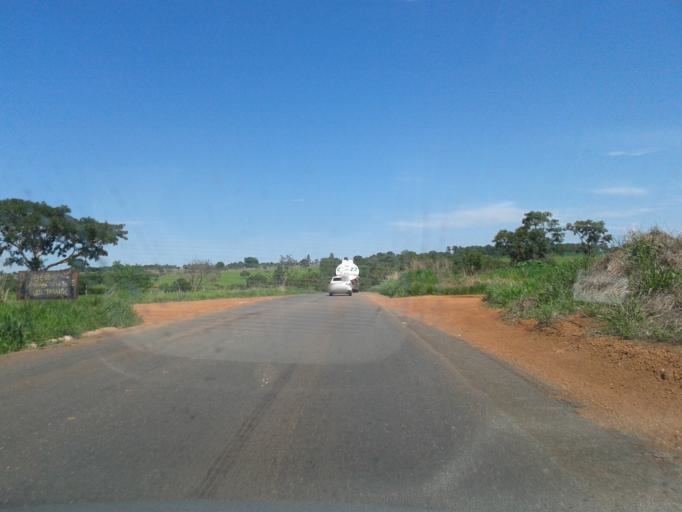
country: BR
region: Goias
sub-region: Bela Vista De Goias
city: Bela Vista de Goias
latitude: -17.0806
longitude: -48.8977
